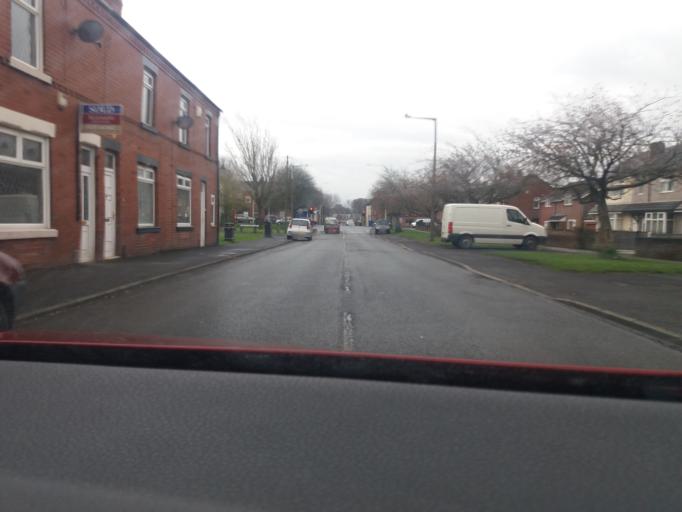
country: GB
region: England
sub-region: Lancashire
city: Chorley
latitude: 53.6443
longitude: -2.6388
